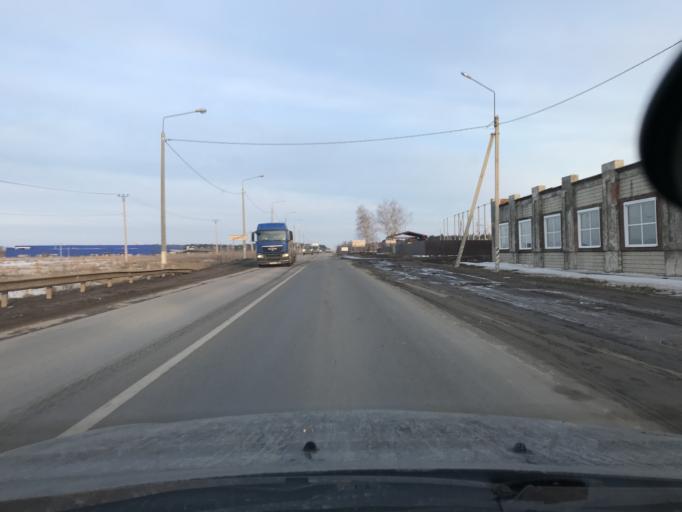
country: RU
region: Kaluga
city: Kaluga
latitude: 54.4676
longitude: 36.2444
